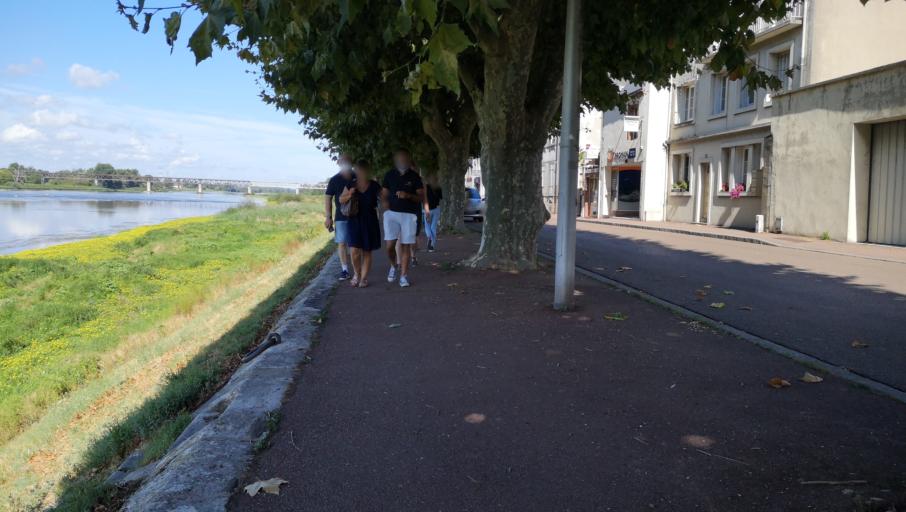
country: FR
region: Centre
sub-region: Departement du Loiret
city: Gien
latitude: 47.6855
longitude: 2.6256
